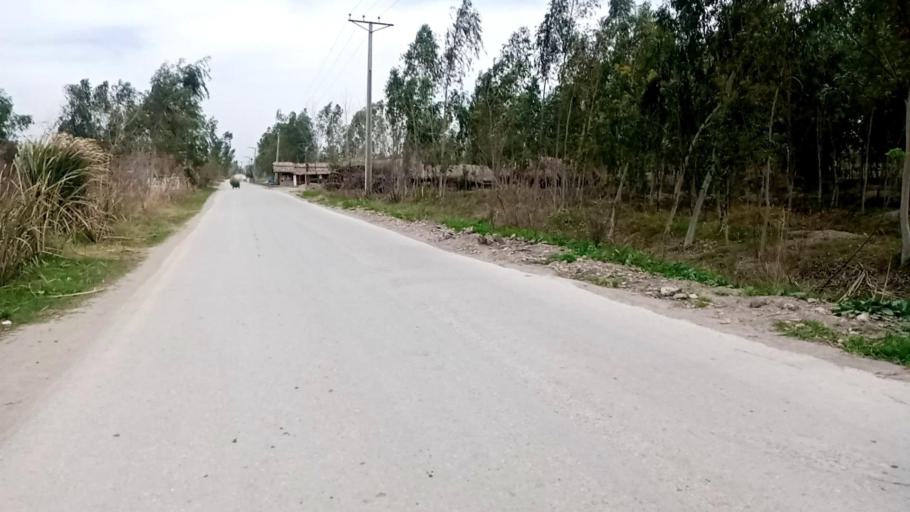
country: PK
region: Khyber Pakhtunkhwa
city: Charsadda
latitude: 34.0625
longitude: 71.6813
